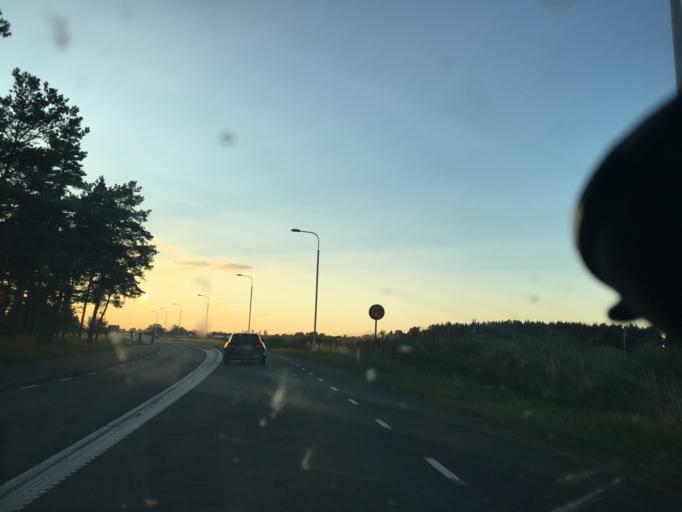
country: SE
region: Skane
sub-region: Kristianstads Kommun
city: Ahus
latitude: 55.9649
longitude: 14.2809
